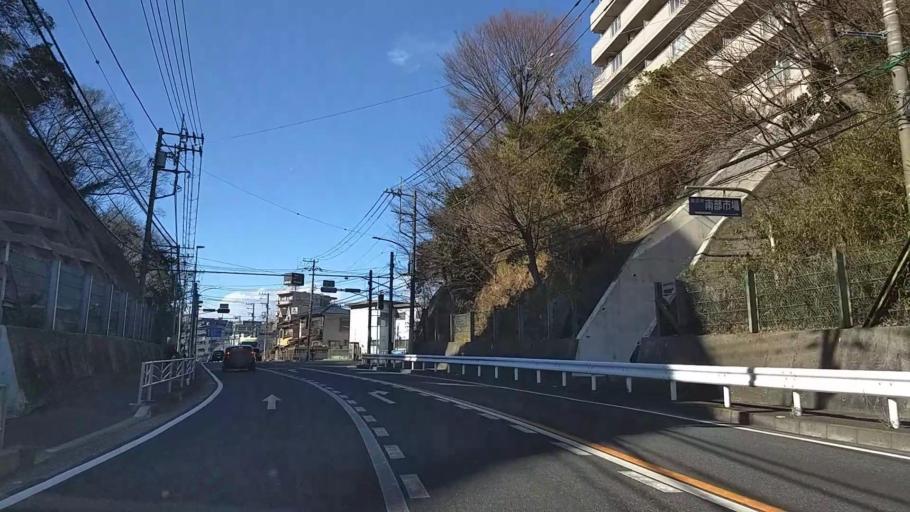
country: JP
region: Kanagawa
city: Yokohama
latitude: 35.3710
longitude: 139.6334
